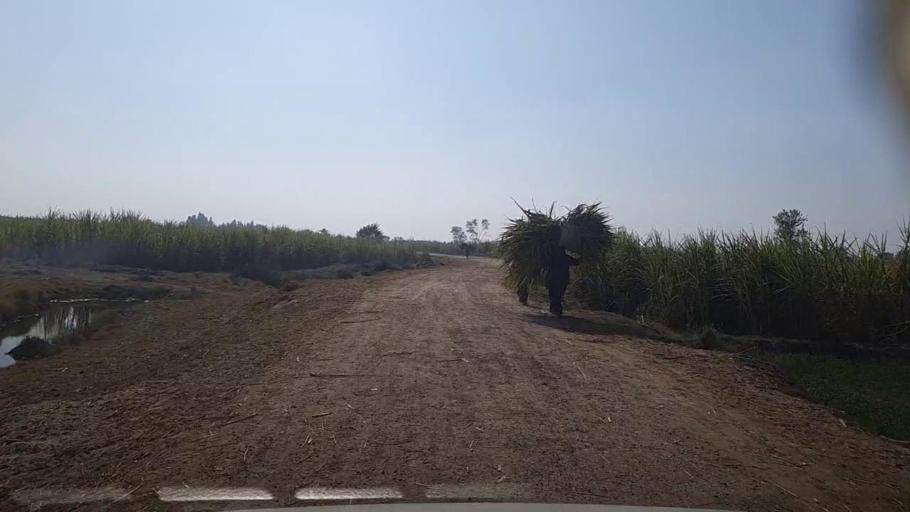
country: PK
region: Sindh
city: Khairpur
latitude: 28.0705
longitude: 69.6176
